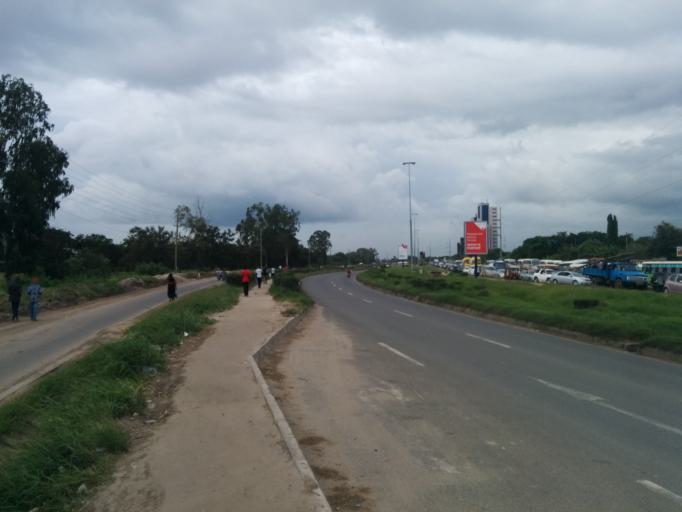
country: TZ
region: Dar es Salaam
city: Magomeni
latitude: -6.7879
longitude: 39.2091
